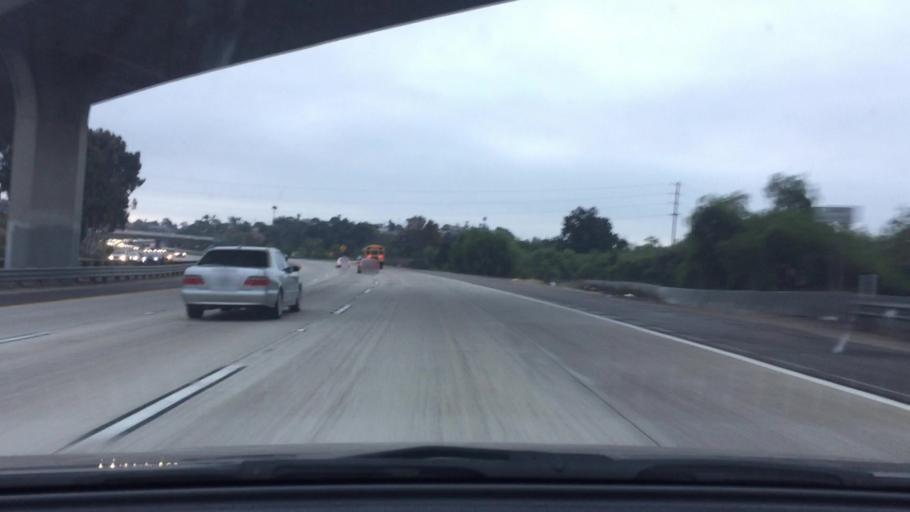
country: US
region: California
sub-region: San Diego County
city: Chula Vista
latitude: 32.6583
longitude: -117.0733
